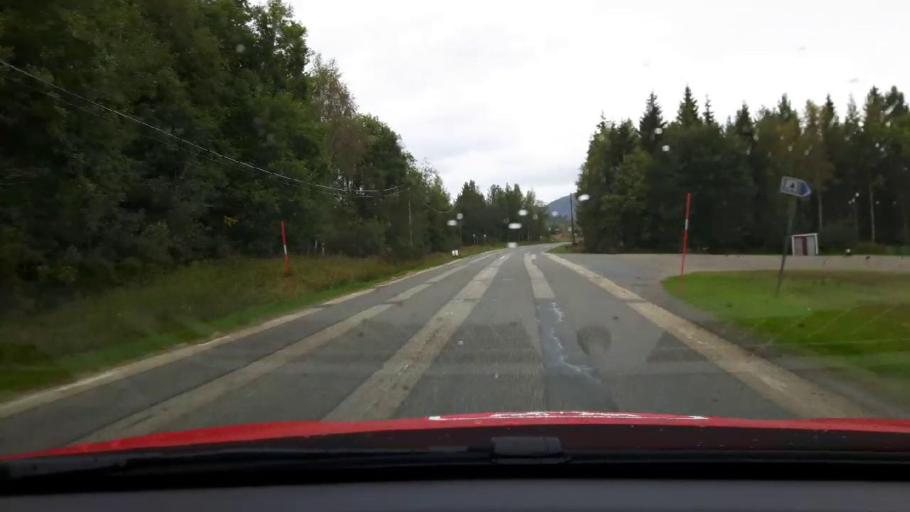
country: SE
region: Jaemtland
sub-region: Bergs Kommun
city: Hoverberg
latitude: 62.7895
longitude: 14.4366
